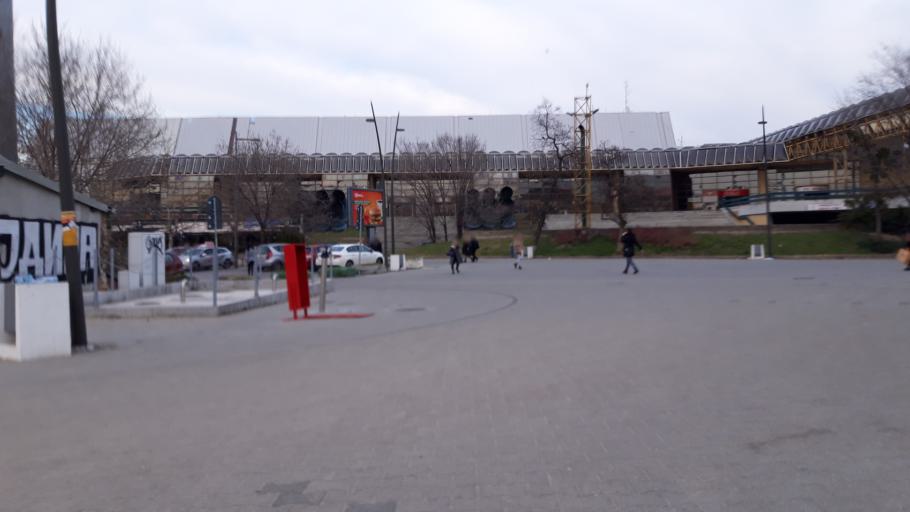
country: RS
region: Autonomna Pokrajina Vojvodina
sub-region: Juznobacki Okrug
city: Novi Sad
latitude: 45.2461
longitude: 19.8432
